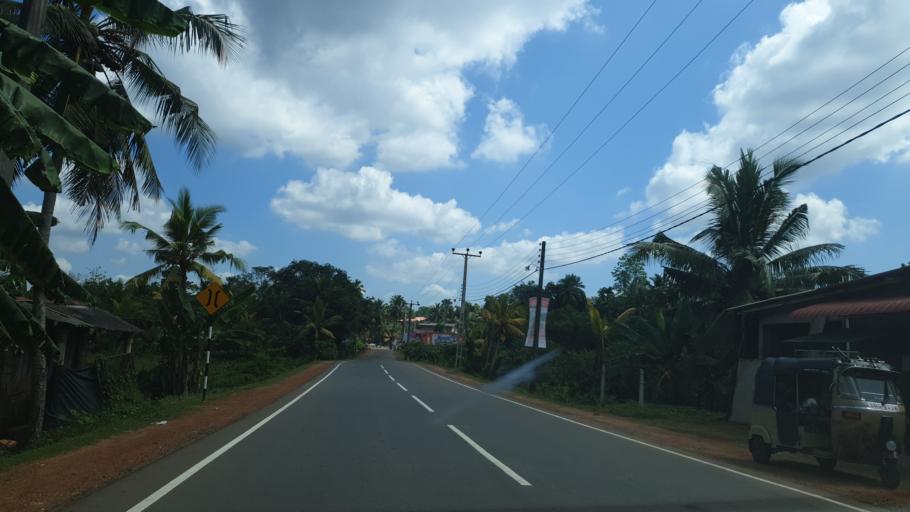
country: LK
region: Western
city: Panadura
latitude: 6.6655
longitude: 79.9568
